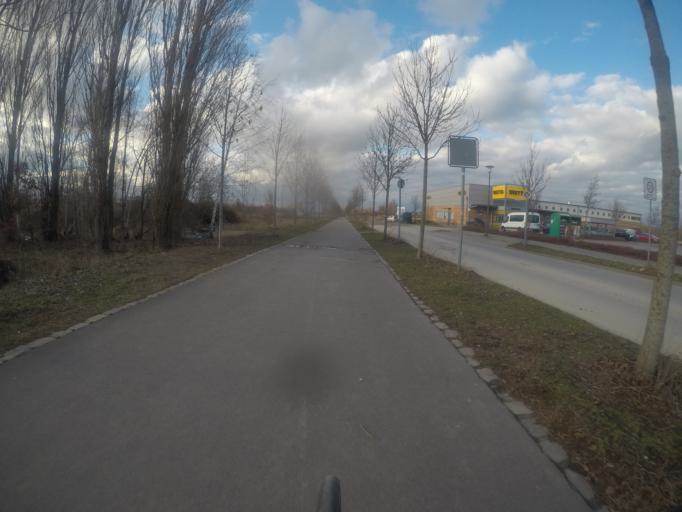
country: DE
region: Brandenburg
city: Ahrensfelde
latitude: 52.5725
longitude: 13.5642
